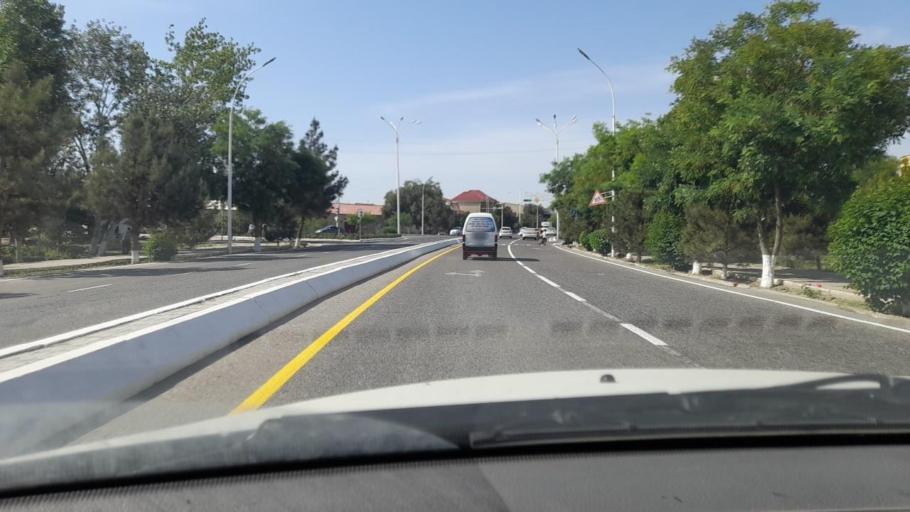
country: UZ
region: Bukhara
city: Bukhara
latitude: 39.7895
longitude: 64.4326
